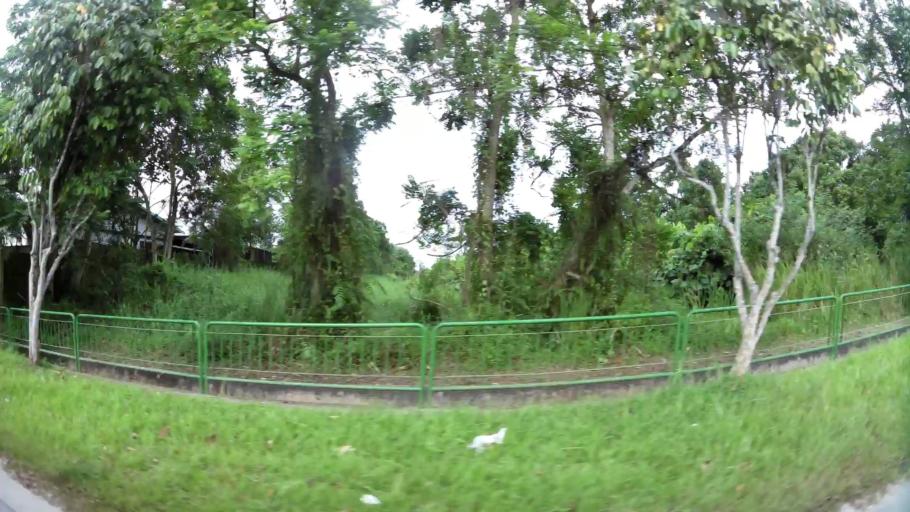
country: MY
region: Johor
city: Johor Bahru
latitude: 1.4290
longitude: 103.7206
